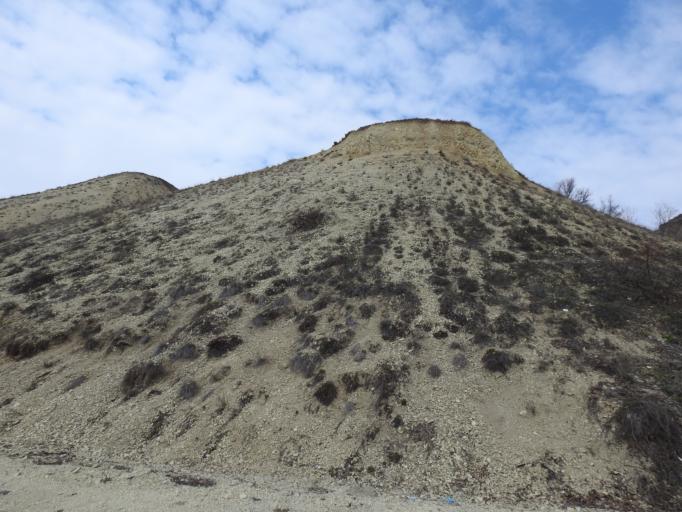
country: RU
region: Saratov
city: Voskresenskoye
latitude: 51.8072
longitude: 46.9182
